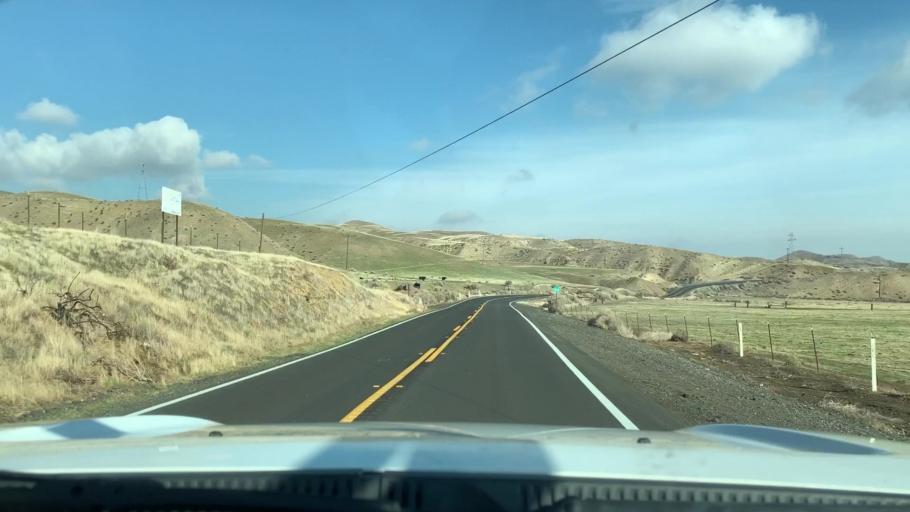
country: US
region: California
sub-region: Fresno County
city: Coalinga
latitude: 36.0945
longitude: -120.4239
